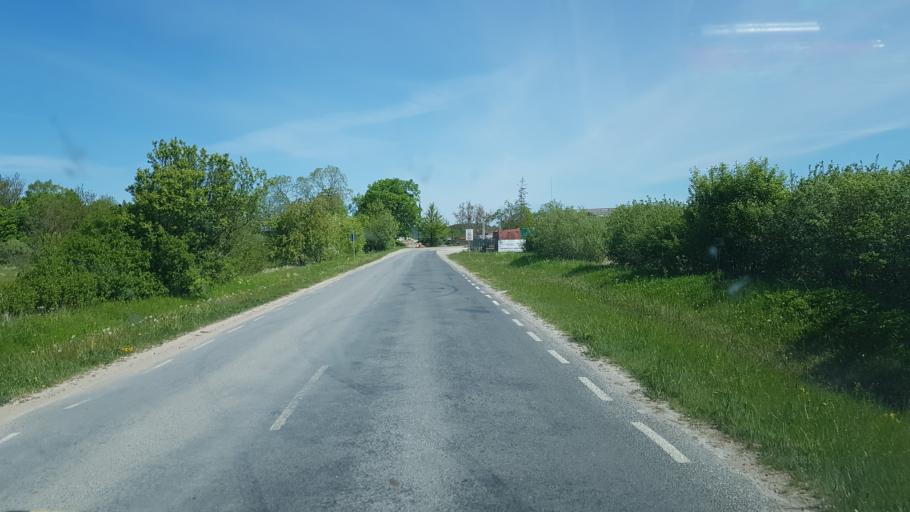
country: EE
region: Saare
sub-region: Kuressaare linn
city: Kuressaare
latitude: 58.2812
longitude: 22.5039
